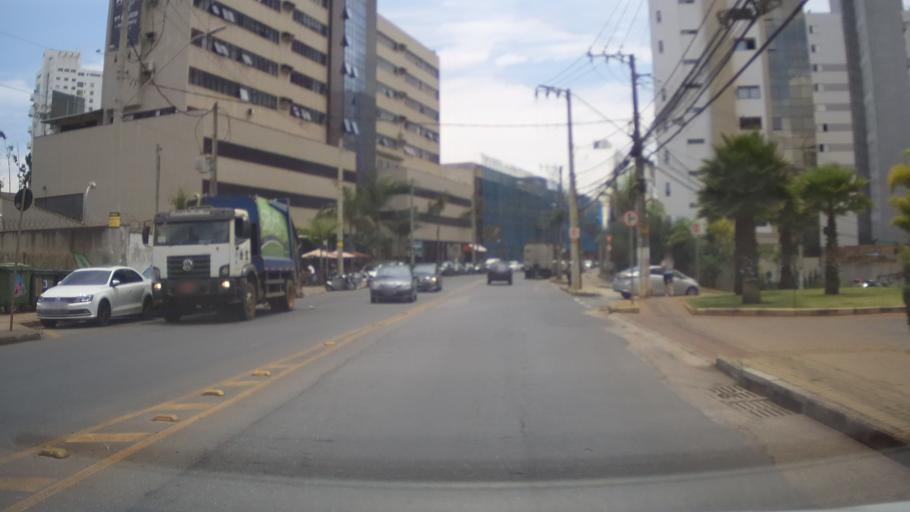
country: BR
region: Minas Gerais
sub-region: Belo Horizonte
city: Belo Horizonte
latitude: -19.9795
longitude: -43.9430
